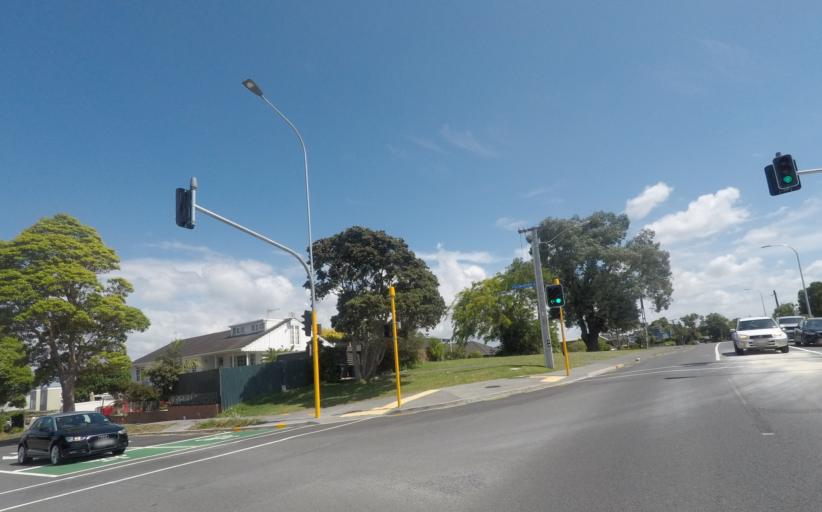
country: NZ
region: Auckland
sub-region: Auckland
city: Tamaki
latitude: -36.8711
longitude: 174.8451
